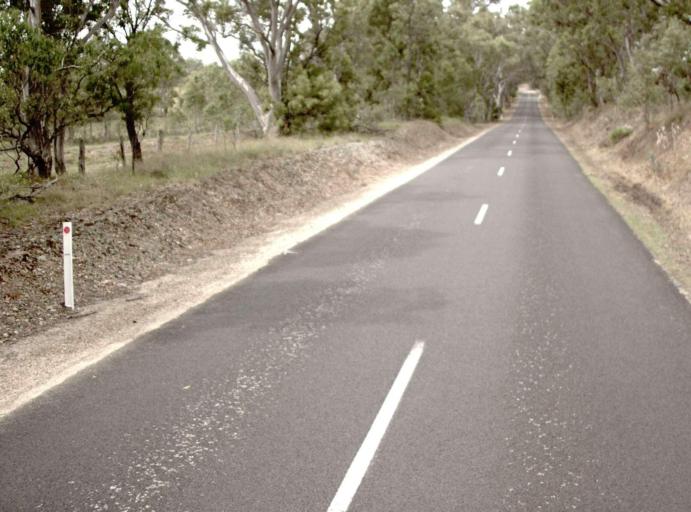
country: AU
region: Victoria
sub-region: Wellington
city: Sale
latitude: -37.8809
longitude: 147.0652
